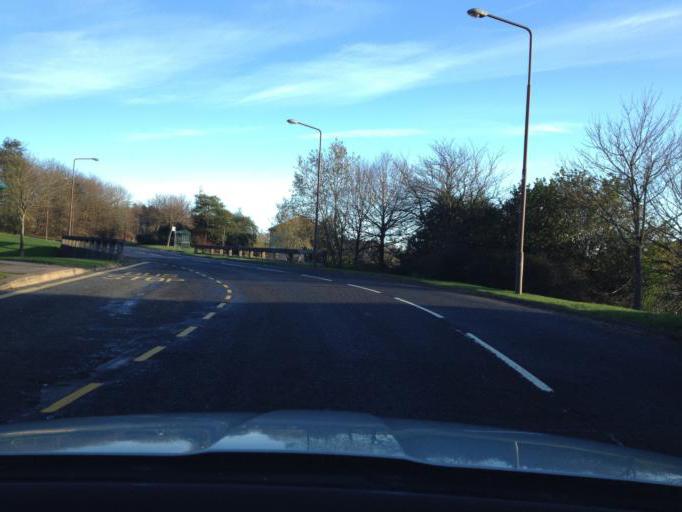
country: GB
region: Scotland
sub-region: West Lothian
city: Livingston
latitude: 55.8992
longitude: -3.5040
